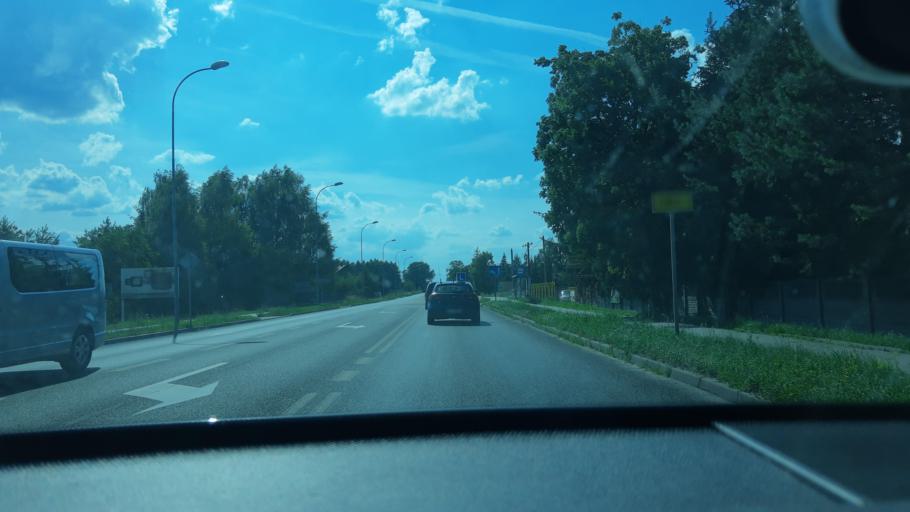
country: PL
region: Lodz Voivodeship
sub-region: Powiat zdunskowolski
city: Zdunska Wola
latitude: 51.6076
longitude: 18.9118
